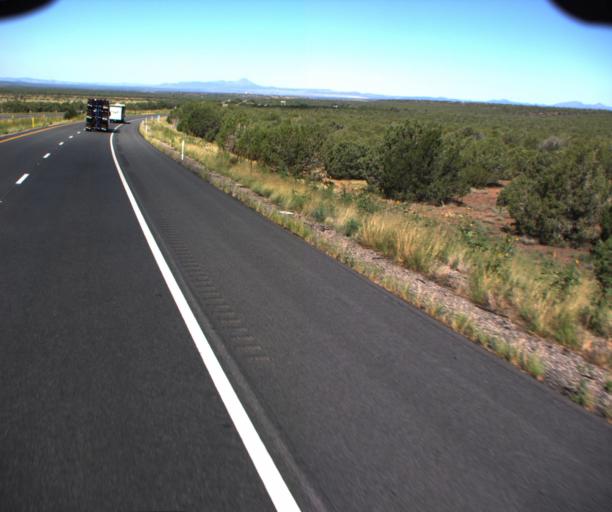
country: US
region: Arizona
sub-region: Coconino County
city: Williams
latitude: 35.2137
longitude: -112.4076
